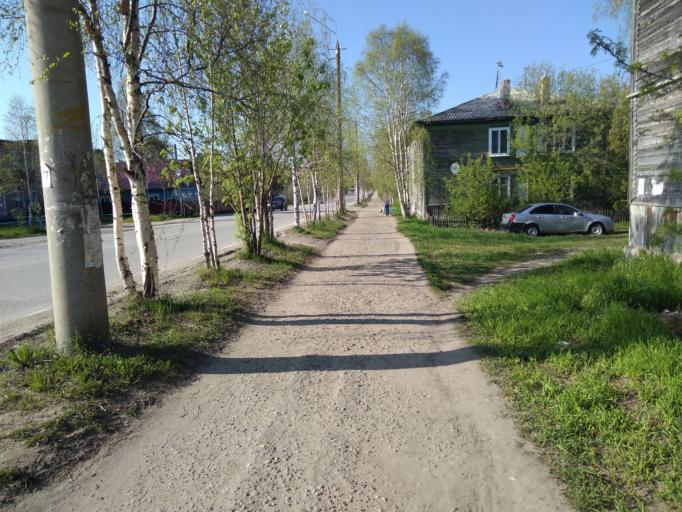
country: RU
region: Komi Republic
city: Pechora
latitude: 65.1198
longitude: 57.1542
